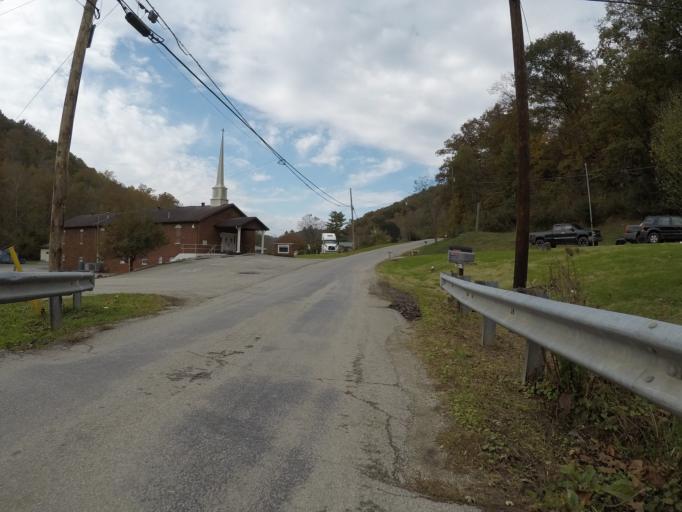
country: US
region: West Virginia
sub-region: Wayne County
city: Lavalette
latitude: 38.3352
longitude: -82.4405
